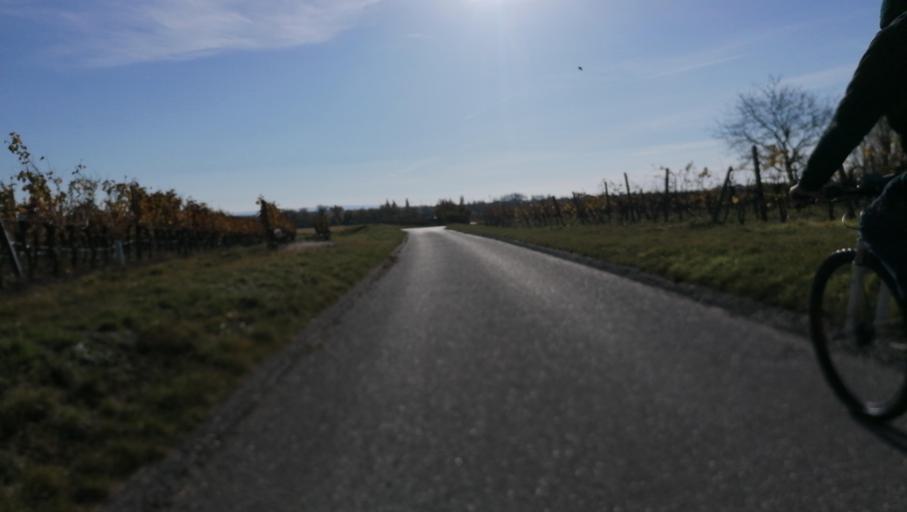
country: AT
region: Lower Austria
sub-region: Politischer Bezirk Modling
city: Gumpoldskirchen
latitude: 48.0354
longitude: 16.2800
